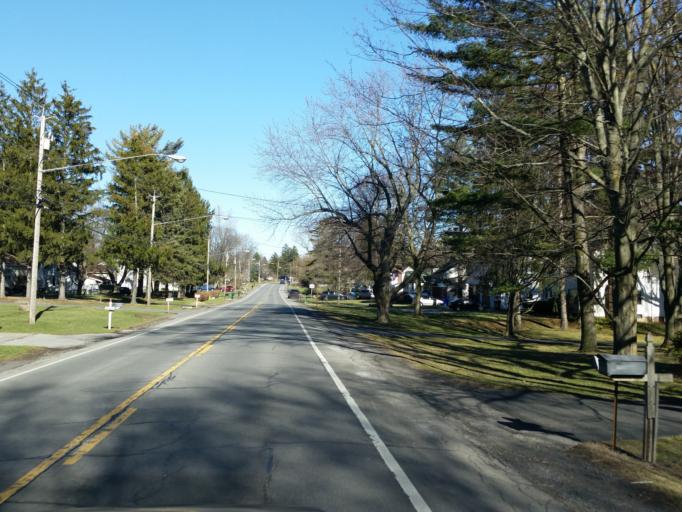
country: US
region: New York
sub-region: Monroe County
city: Scottsville
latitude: 43.0935
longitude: -77.7953
